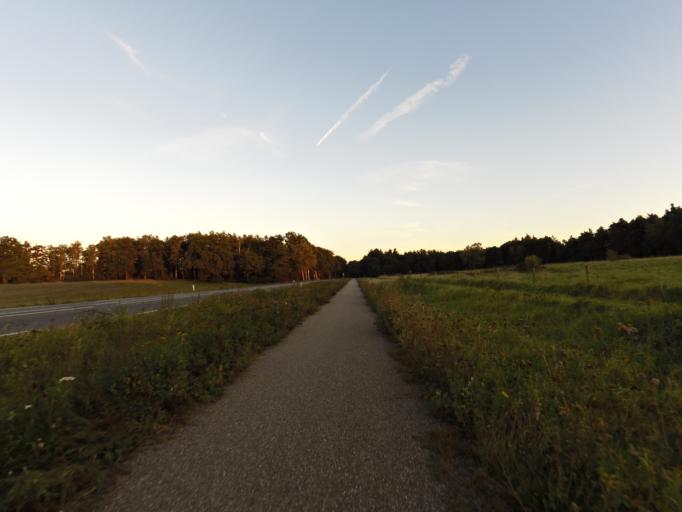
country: NL
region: Gelderland
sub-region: Gemeente Montferland
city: s-Heerenberg
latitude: 51.9024
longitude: 6.2437
